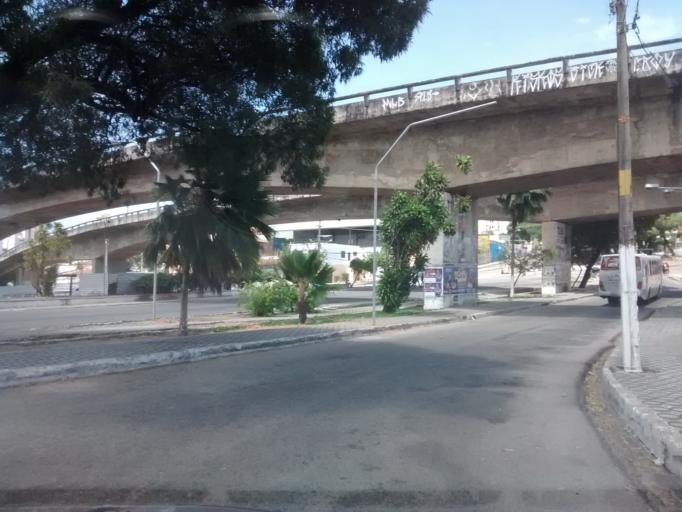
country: BR
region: Rio Grande do Norte
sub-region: Natal
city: Natal
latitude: -5.7906
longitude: -35.2091
